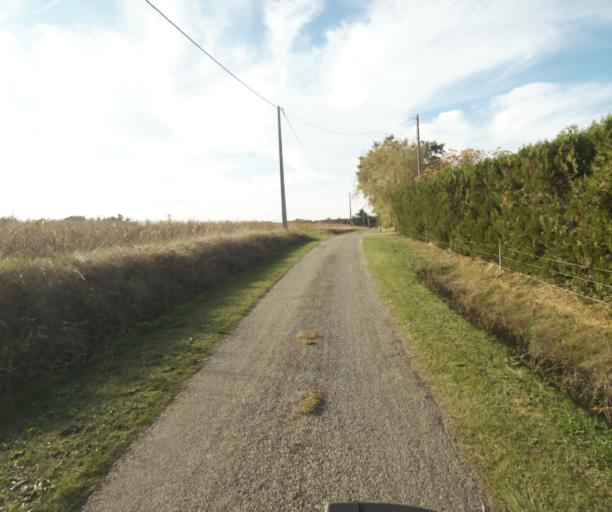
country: FR
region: Midi-Pyrenees
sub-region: Departement du Tarn-et-Garonne
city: Finhan
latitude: 43.9121
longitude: 1.1070
